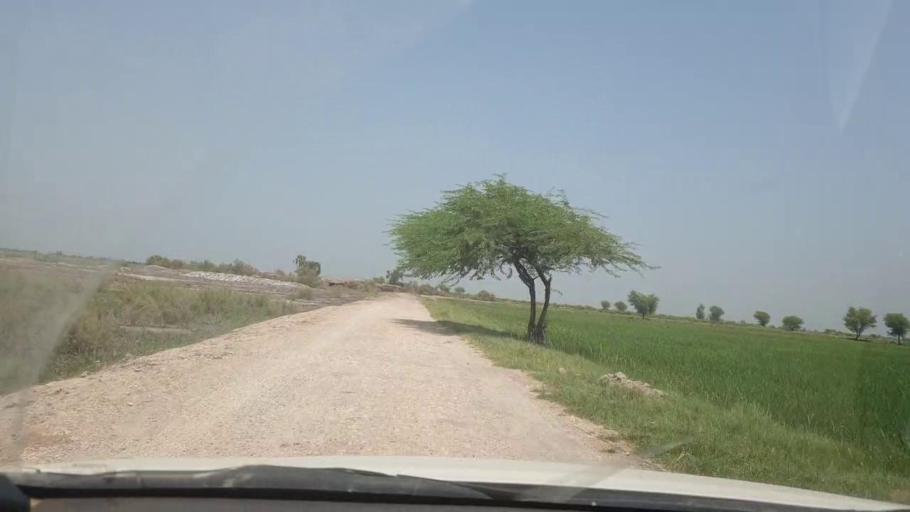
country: PK
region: Sindh
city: Lakhi
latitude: 27.8830
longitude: 68.7396
